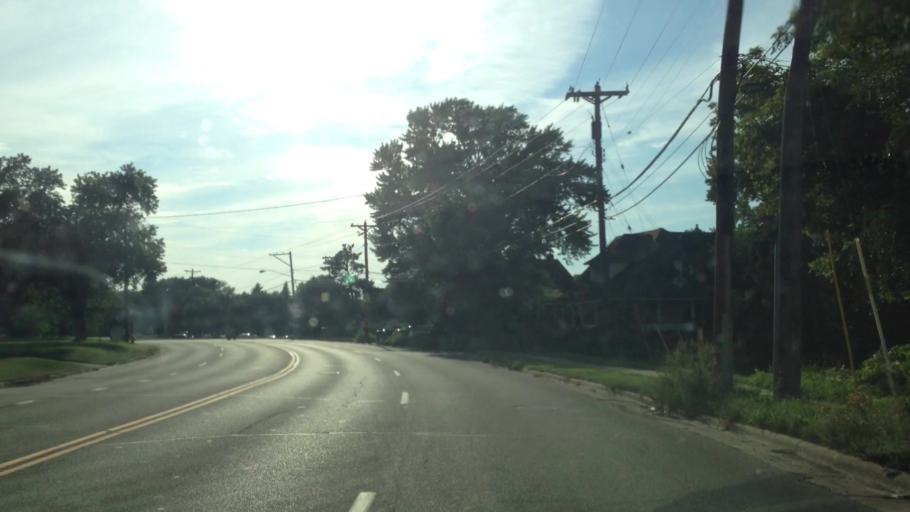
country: US
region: Minnesota
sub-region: Ramsey County
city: New Brighton
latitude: 45.0655
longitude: -93.1955
